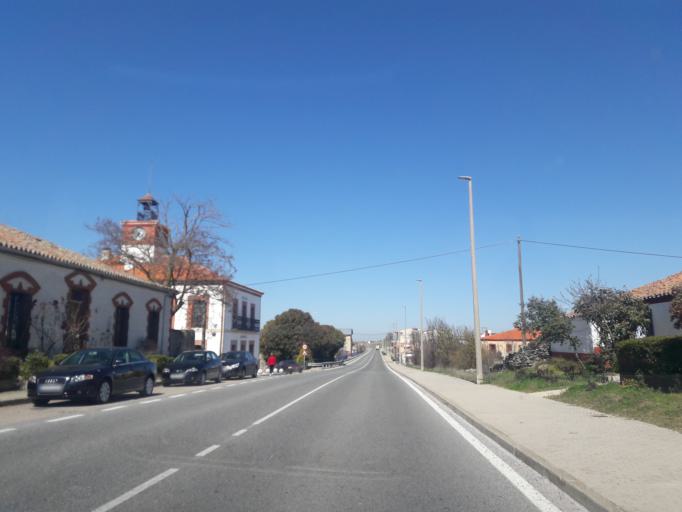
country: ES
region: Castille and Leon
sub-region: Provincia de Salamanca
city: Mozarbez
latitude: 40.8565
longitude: -5.6504
